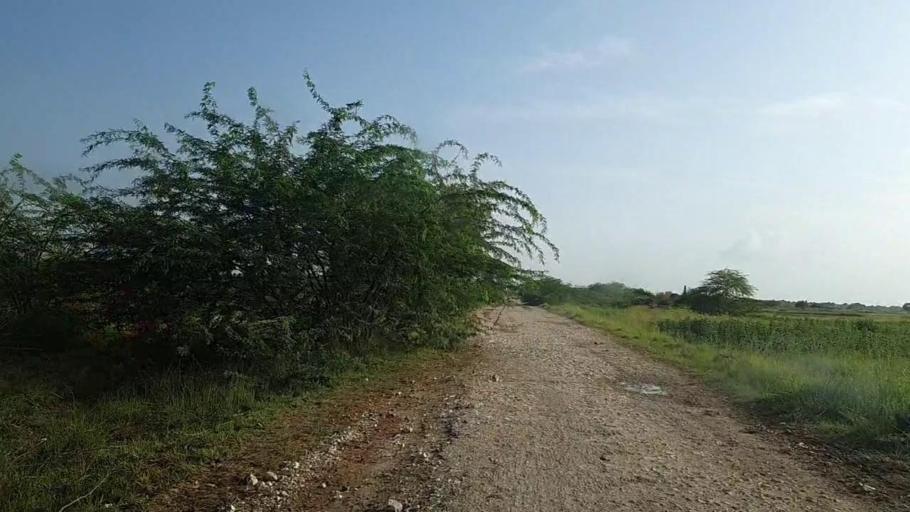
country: PK
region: Sindh
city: Pad Idan
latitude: 26.8141
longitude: 68.2366
